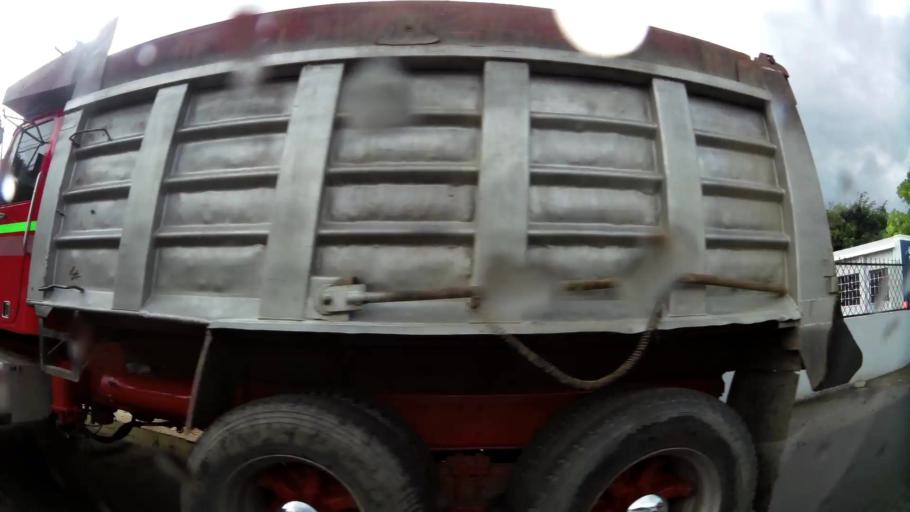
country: DO
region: Monsenor Nouel
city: Bonao
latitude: 18.9340
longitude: -70.3986
